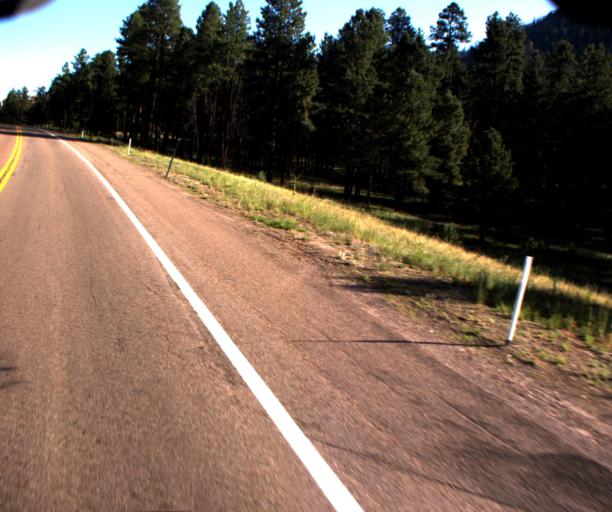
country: US
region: Arizona
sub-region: Apache County
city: Eagar
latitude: 33.8946
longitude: -109.1545
